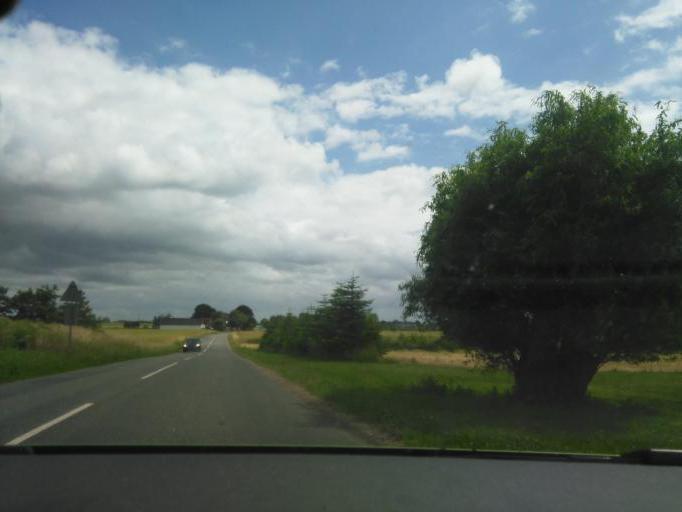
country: DK
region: Zealand
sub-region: Kalundborg Kommune
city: Gorlev
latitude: 55.5492
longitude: 11.1848
